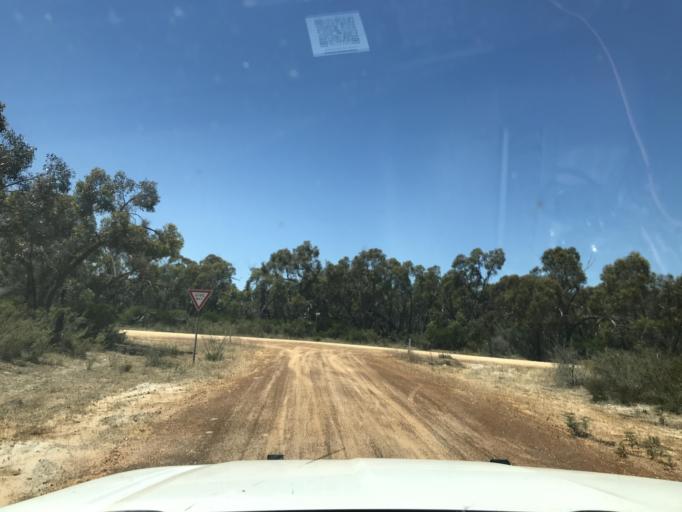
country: AU
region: South Australia
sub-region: Wattle Range
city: Penola
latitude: -37.0468
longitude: 141.3967
